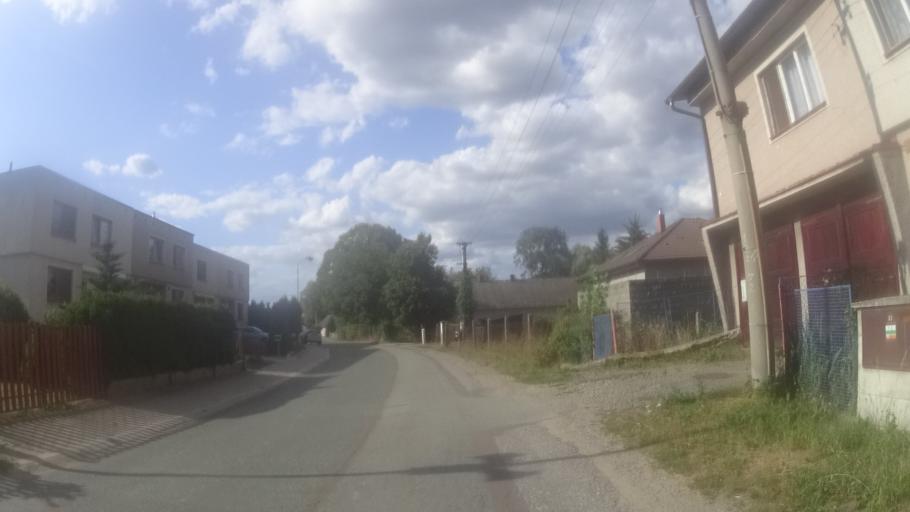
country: CZ
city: Albrechtice nad Orlici
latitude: 50.1469
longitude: 16.0608
